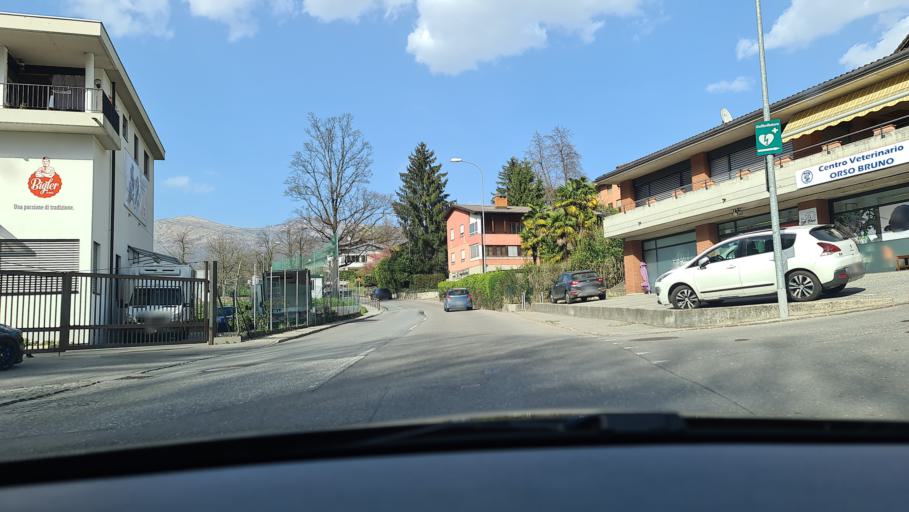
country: CH
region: Ticino
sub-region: Lugano District
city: Canobbio
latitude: 46.0372
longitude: 8.9770
